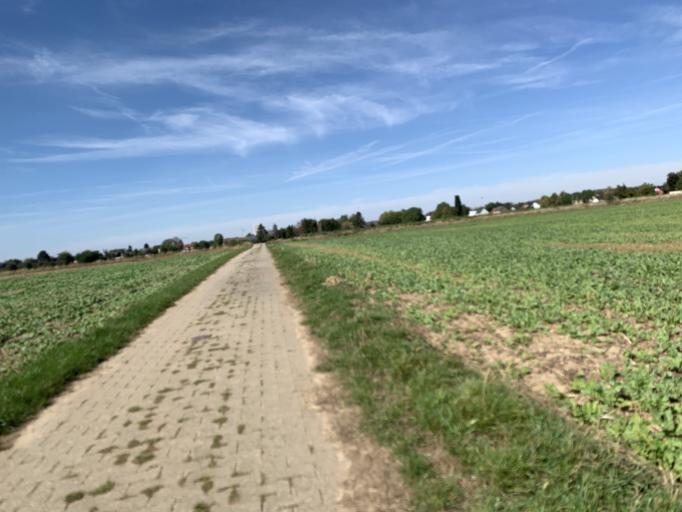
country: DE
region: North Rhine-Westphalia
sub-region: Regierungsbezirk Koln
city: Dueren
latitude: 50.7947
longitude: 6.4357
